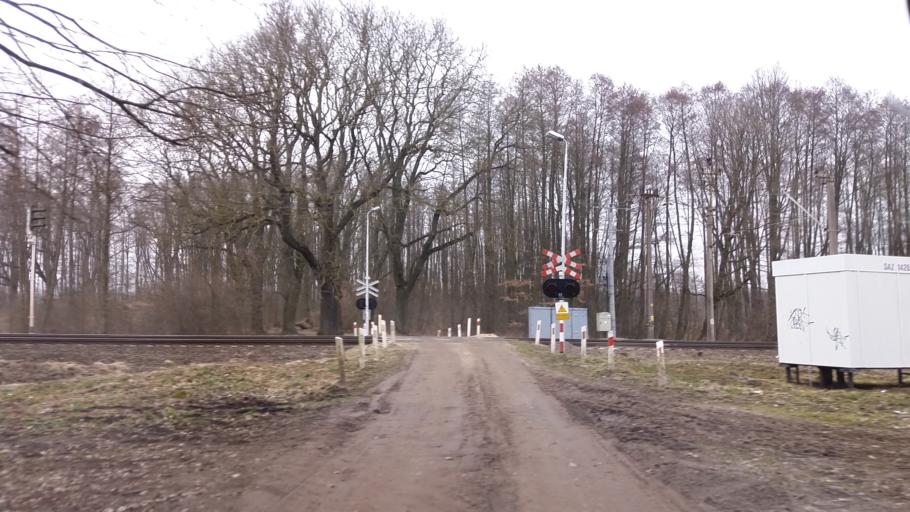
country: PL
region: West Pomeranian Voivodeship
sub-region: Powiat choszczenski
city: Choszczno
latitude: 53.1635
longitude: 15.3463
